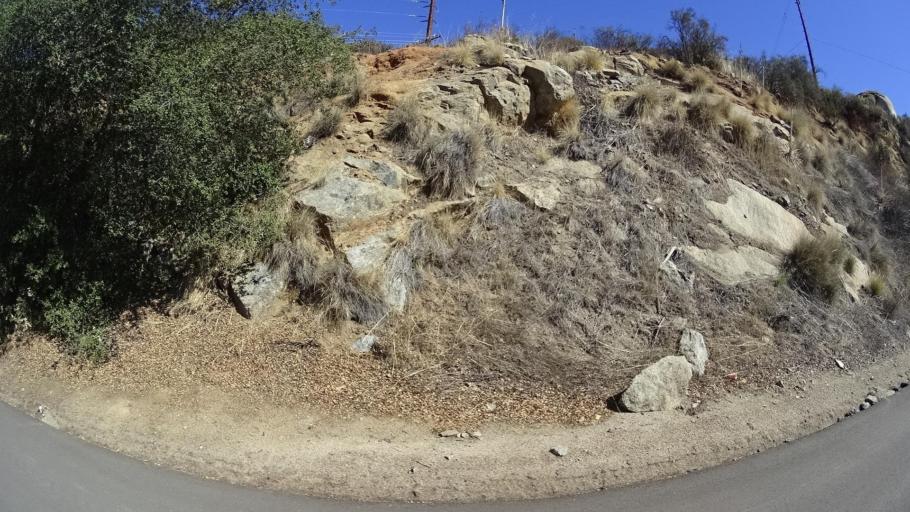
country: US
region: California
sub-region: San Diego County
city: Alpine
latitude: 32.7680
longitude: -116.6952
